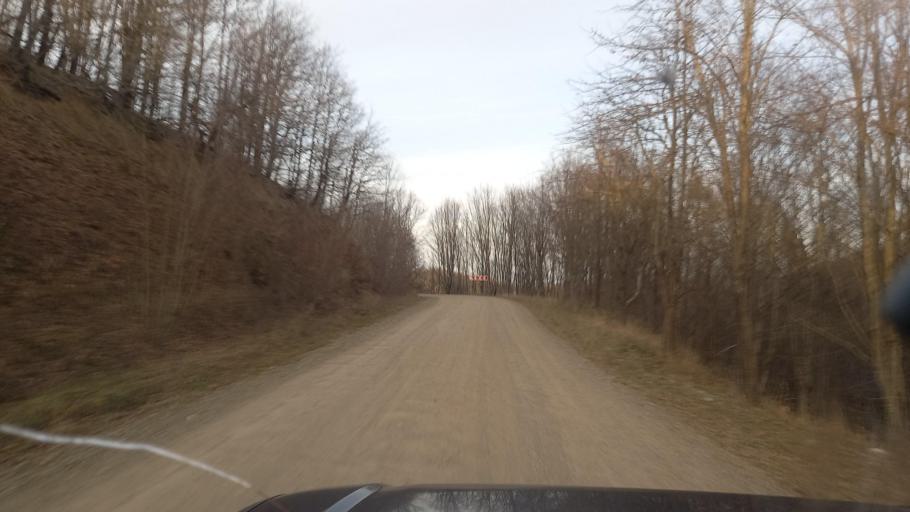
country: RU
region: Krasnodarskiy
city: Goryachiy Klyuch
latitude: 44.3633
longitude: 39.2200
